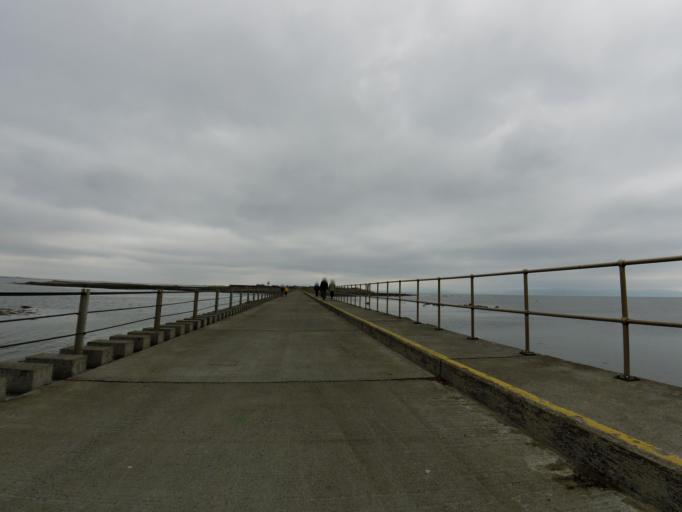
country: IE
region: Connaught
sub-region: County Galway
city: Gaillimh
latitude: 53.2590
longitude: -9.0555
